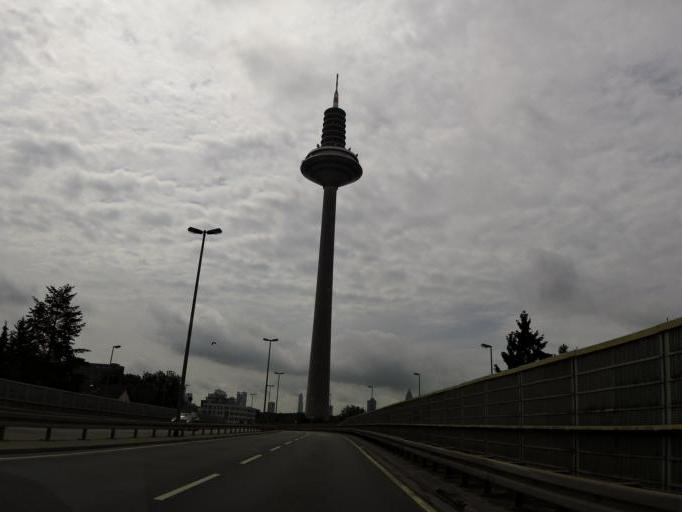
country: DE
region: Hesse
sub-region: Regierungsbezirk Darmstadt
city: Frankfurt am Main
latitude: 50.1388
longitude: 8.6536
